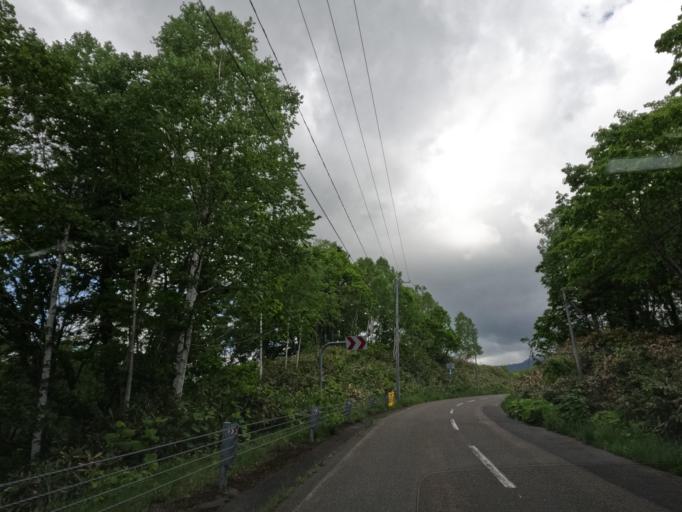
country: JP
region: Hokkaido
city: Tobetsu
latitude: 43.4610
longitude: 141.5952
